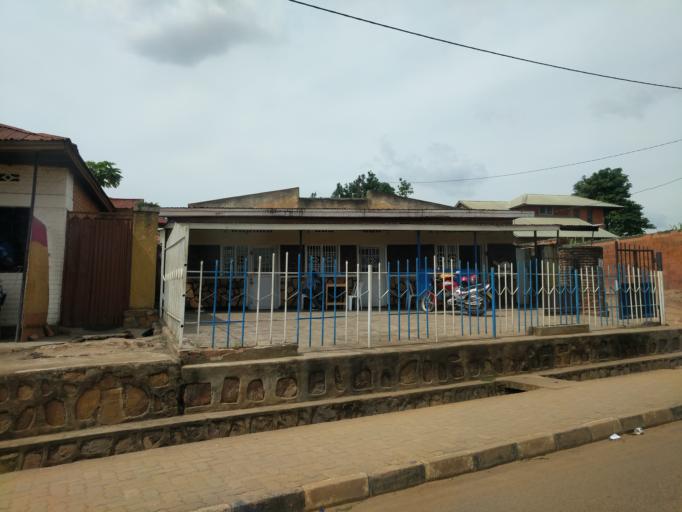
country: RW
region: Kigali
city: Kigali
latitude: -1.9705
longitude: 30.1270
